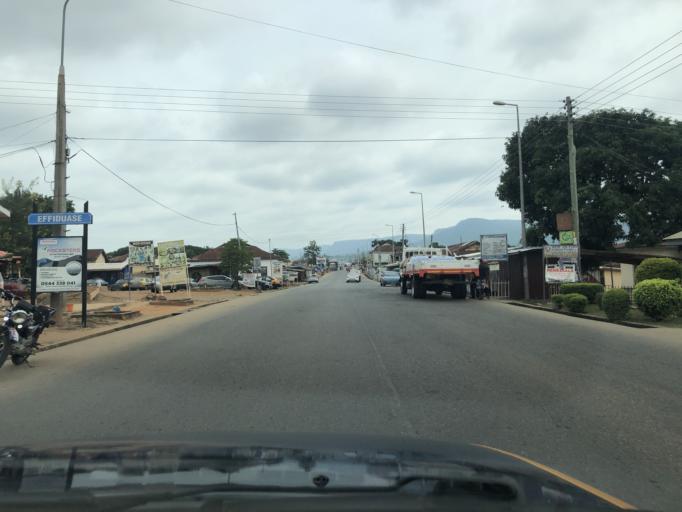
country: GH
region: Eastern
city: Koforidua
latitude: 6.1044
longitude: -0.2670
